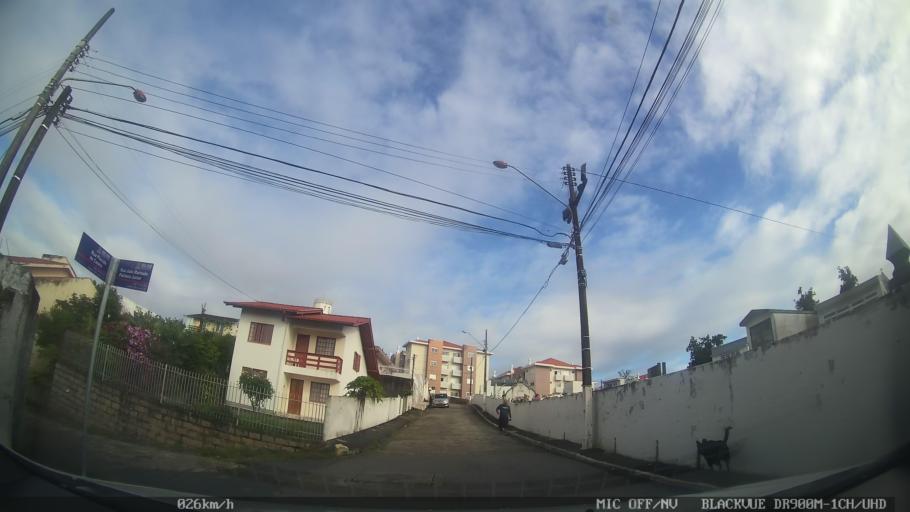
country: BR
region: Santa Catarina
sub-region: Sao Jose
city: Campinas
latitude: -27.6121
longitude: -48.6287
